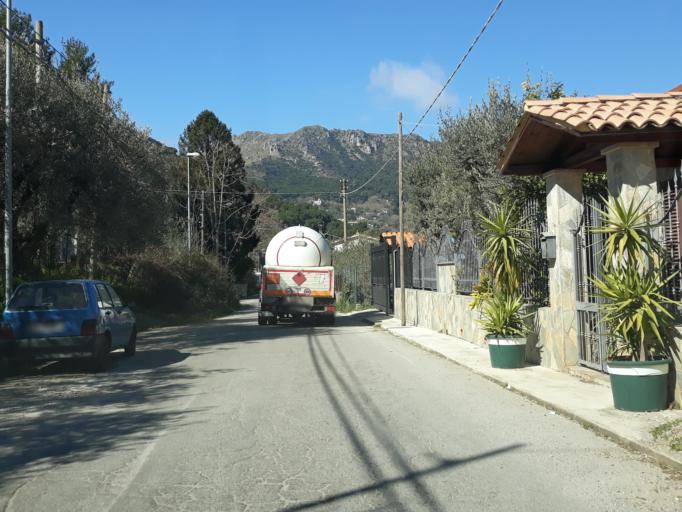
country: IT
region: Sicily
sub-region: Palermo
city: Piano dei Geli
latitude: 38.0854
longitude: 13.2631
